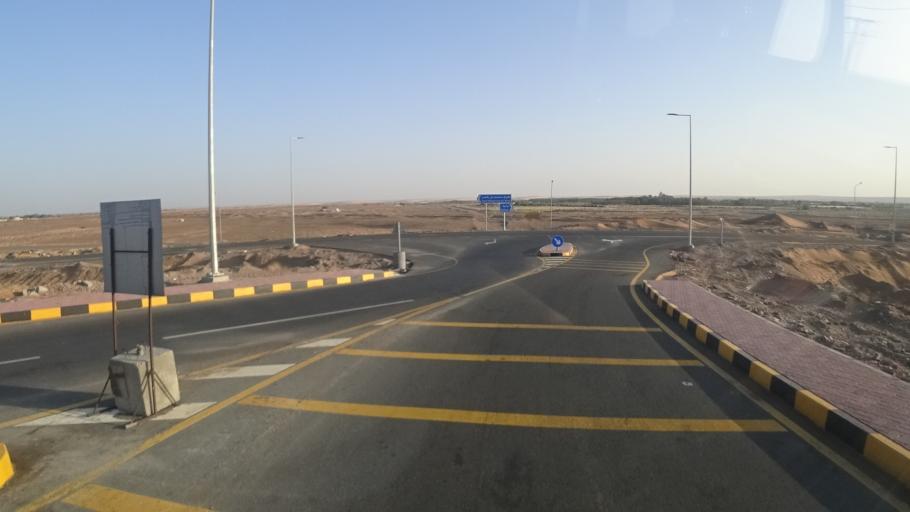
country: OM
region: Ash Sharqiyah
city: Badiyah
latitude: 22.4641
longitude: 58.8623
